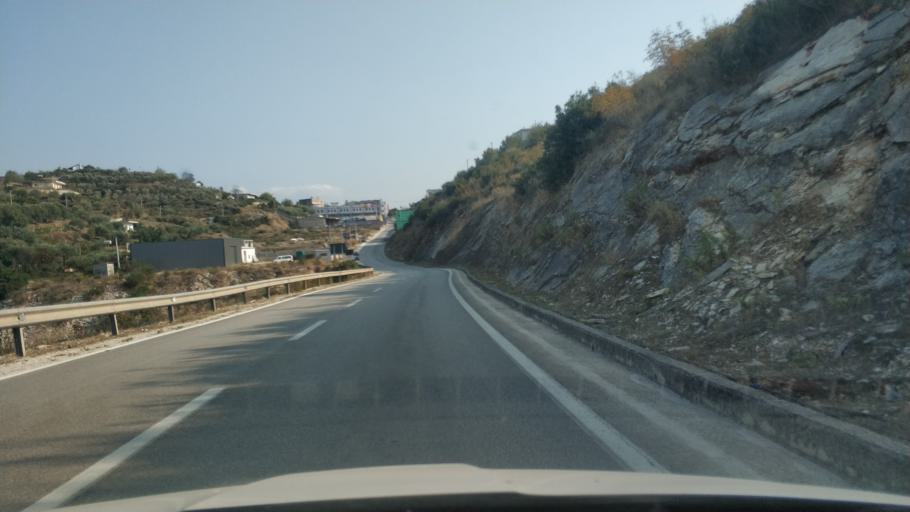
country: AL
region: Vlore
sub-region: Rrethi i Sarandes
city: Sarande
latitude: 39.8814
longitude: 20.0218
